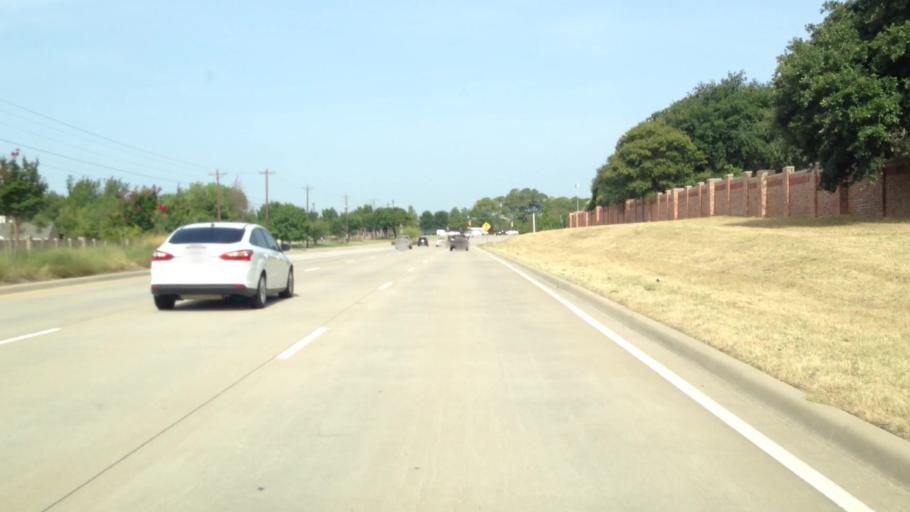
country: US
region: Texas
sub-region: Denton County
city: Flower Mound
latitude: 33.0101
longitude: -97.0412
